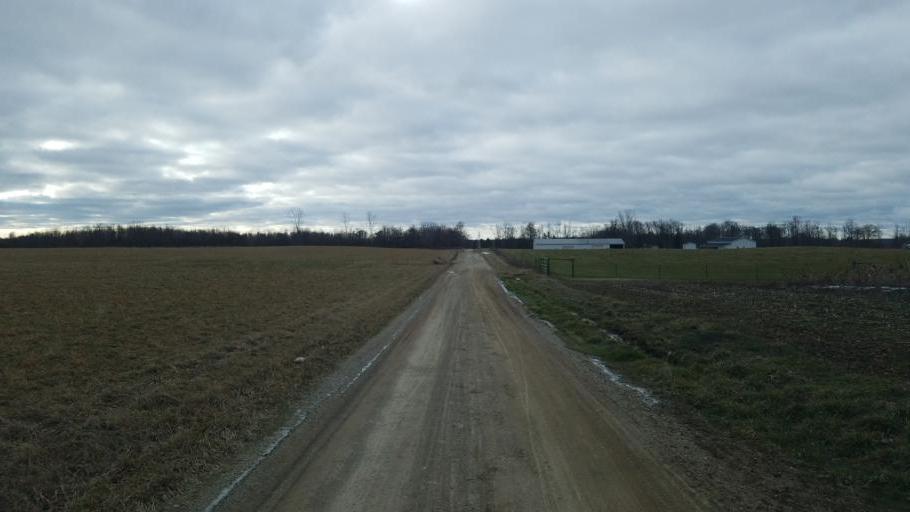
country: US
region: Ohio
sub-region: Richland County
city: Lexington
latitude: 40.5785
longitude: -82.6764
